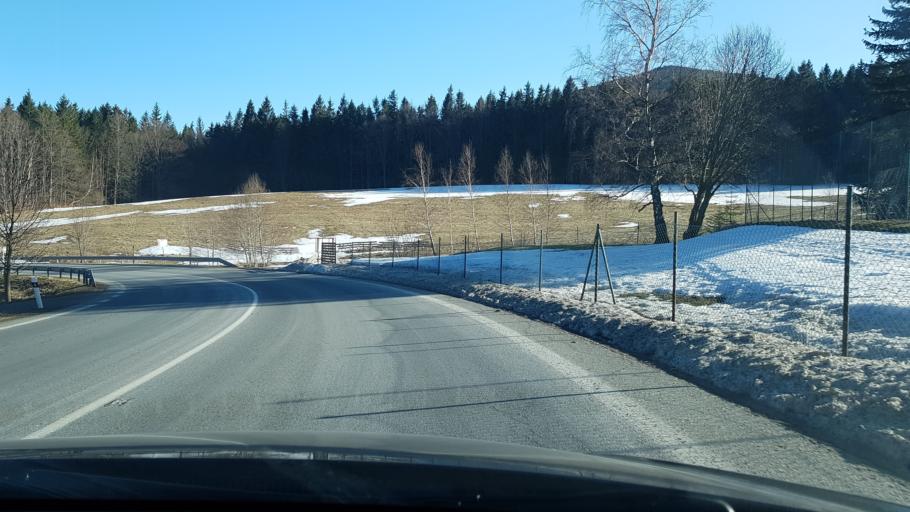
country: CZ
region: Olomoucky
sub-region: Okres Jesenik
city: Jesenik
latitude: 50.1561
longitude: 17.1725
